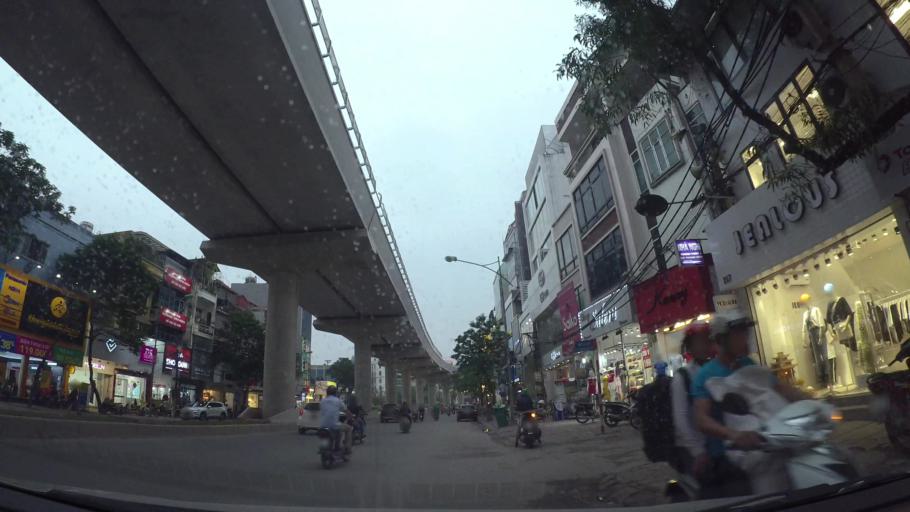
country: VN
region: Ha Noi
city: Cau Giay
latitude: 21.0345
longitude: 105.7957
